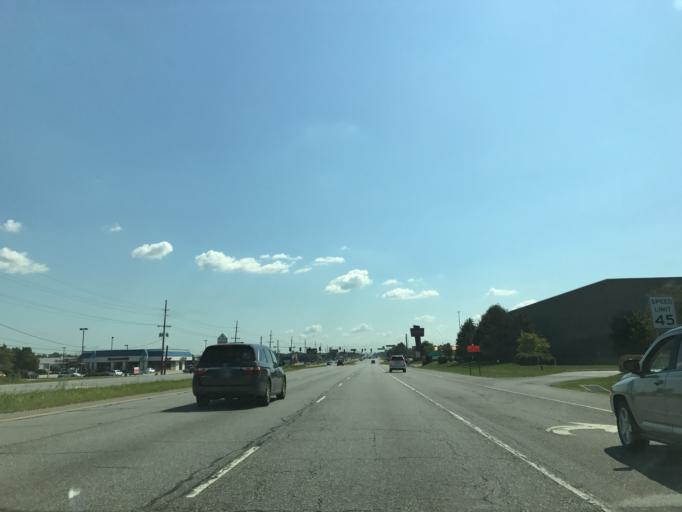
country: US
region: Indiana
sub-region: Lake County
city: Merrillville
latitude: 41.4712
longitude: -87.3161
